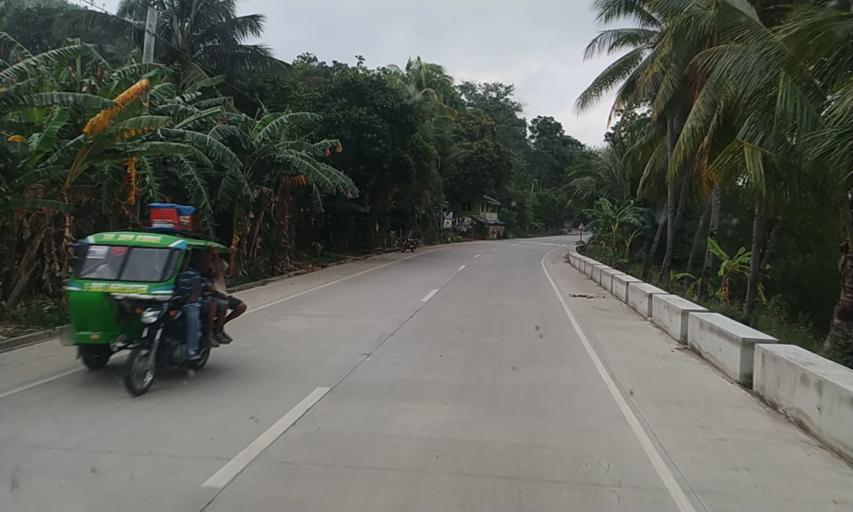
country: PH
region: Central Visayas
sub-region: Province of Negros Oriental
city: Basak
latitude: 10.2019
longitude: 123.2995
